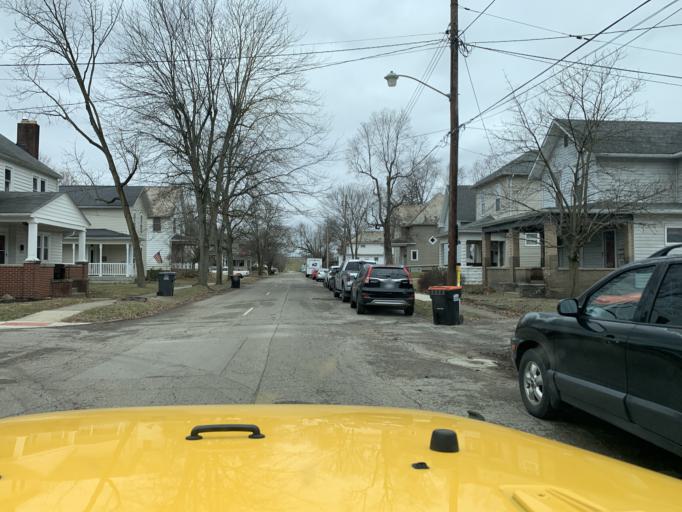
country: US
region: Ohio
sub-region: Licking County
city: Newark
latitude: 40.0588
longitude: -82.4127
